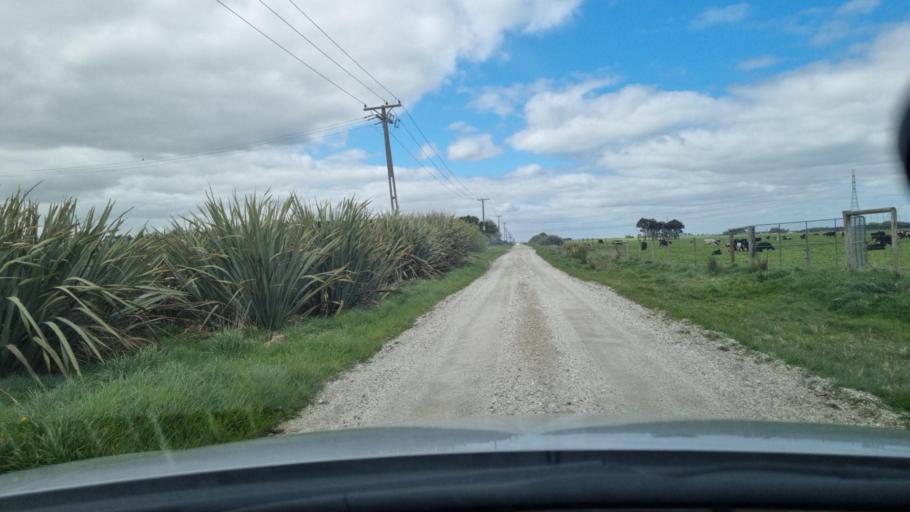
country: NZ
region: Southland
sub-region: Invercargill City
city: Invercargill
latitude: -46.4428
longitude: 168.4347
